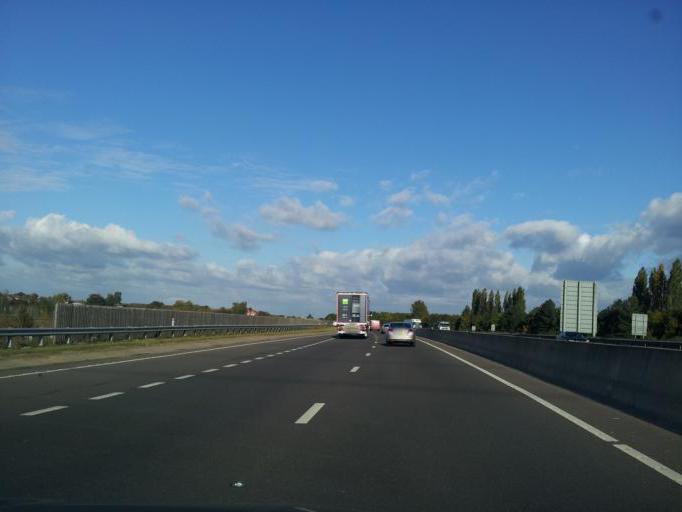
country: GB
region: England
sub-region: Central Bedfordshire
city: Marston Moretaine
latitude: 52.0685
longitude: -0.5480
